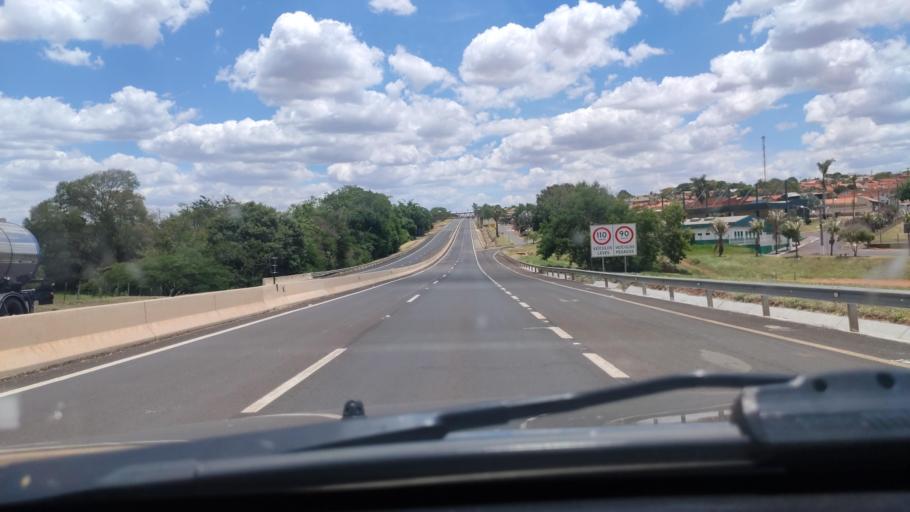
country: BR
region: Sao Paulo
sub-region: Duartina
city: Duartina
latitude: -22.6956
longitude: -49.4272
